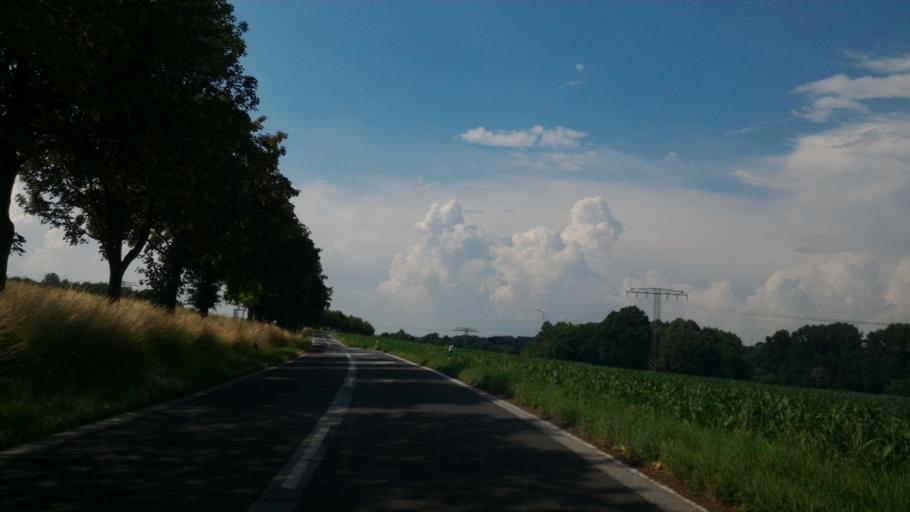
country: DE
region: Saxony
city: Hirschfelde
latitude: 50.9276
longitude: 14.8623
